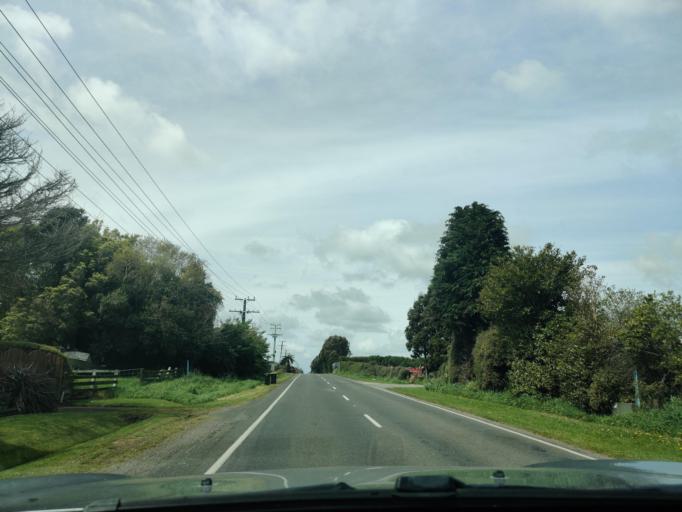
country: NZ
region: Taranaki
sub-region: South Taranaki District
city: Eltham
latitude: -39.4285
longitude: 174.1573
